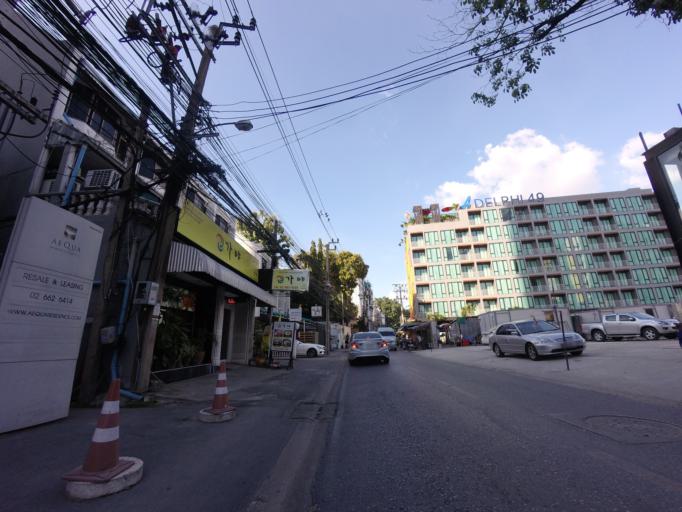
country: TH
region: Bangkok
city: Watthana
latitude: 13.7277
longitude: 100.5755
